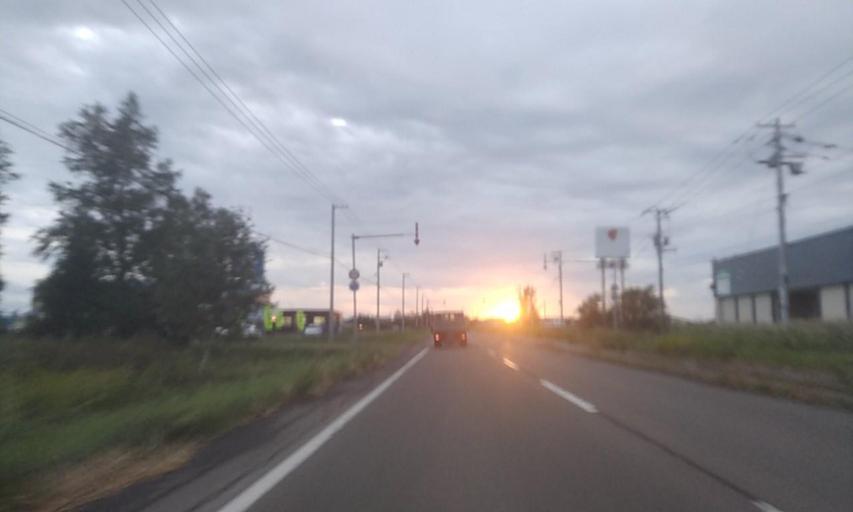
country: JP
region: Hokkaido
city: Abashiri
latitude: 43.9002
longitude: 144.6500
